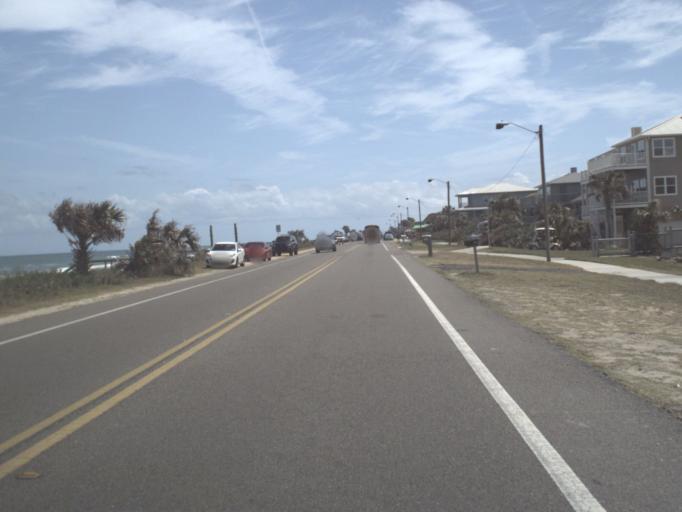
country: US
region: Florida
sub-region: Flagler County
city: Flagler Beach
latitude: 29.4900
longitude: -81.1319
